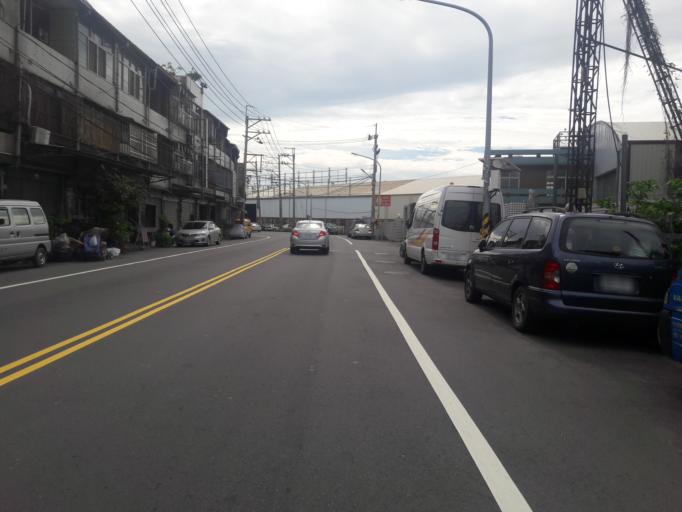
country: TW
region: Taiwan
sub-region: Taichung City
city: Taichung
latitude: 24.0969
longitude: 120.6971
